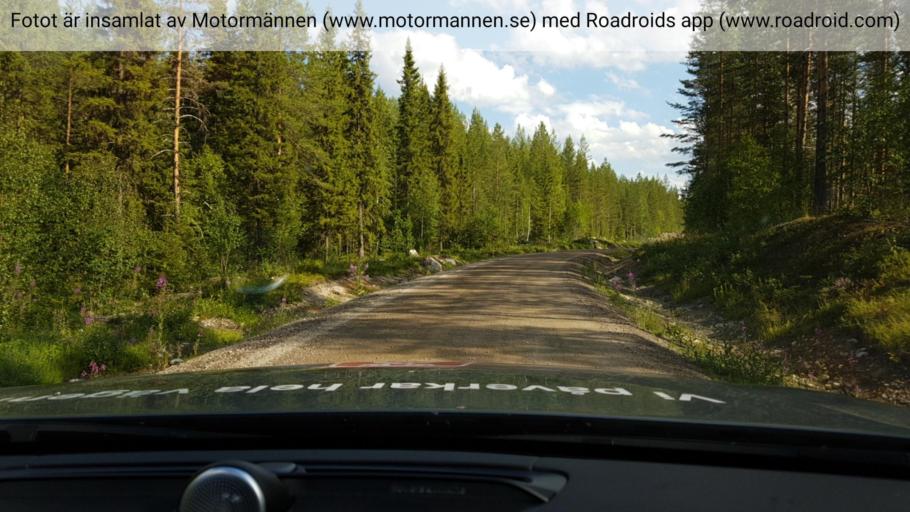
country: SE
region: Vaesterbotten
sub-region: Dorotea Kommun
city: Dorotea
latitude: 63.9719
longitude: 16.0640
